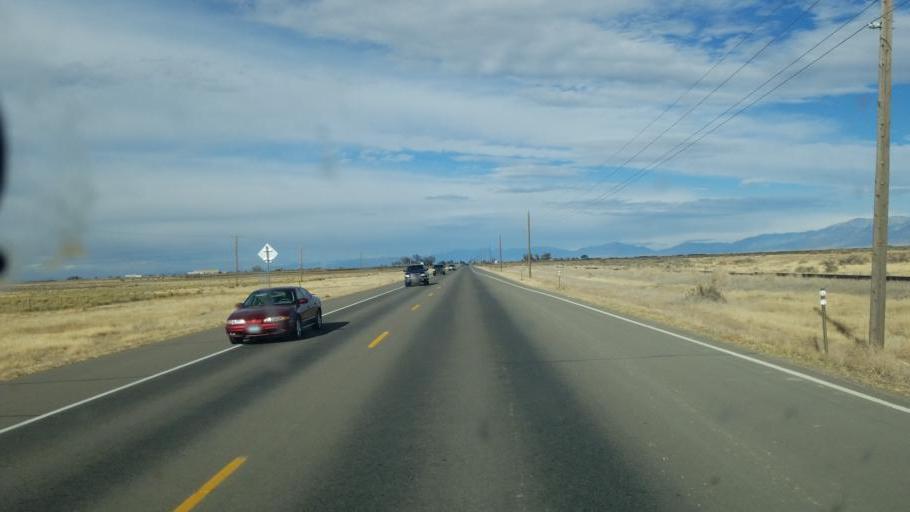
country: US
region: Colorado
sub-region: Alamosa County
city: Alamosa
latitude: 37.3353
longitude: -105.9408
